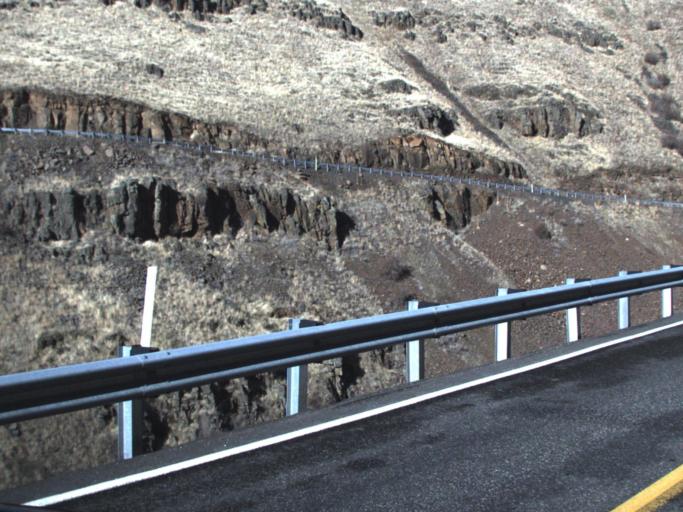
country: US
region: Washington
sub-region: Asotin County
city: Asotin
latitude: 46.0527
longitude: -117.2304
